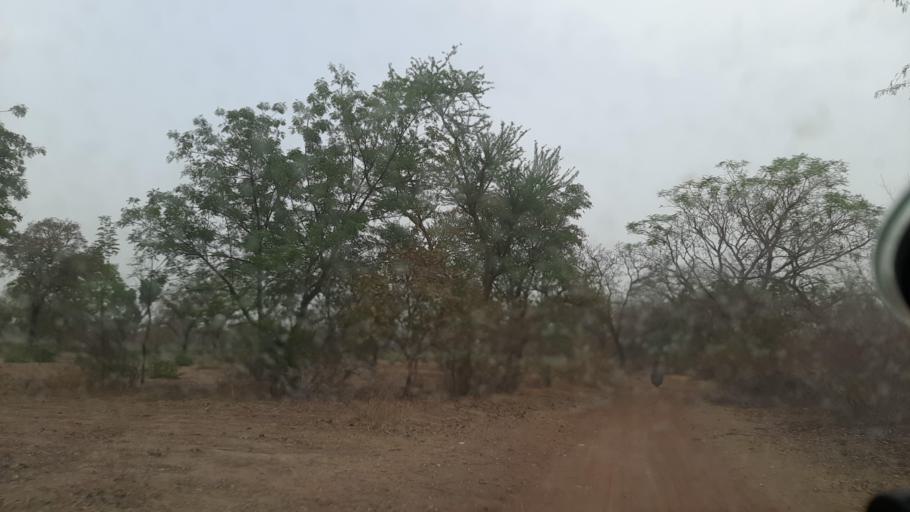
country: BF
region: Boucle du Mouhoun
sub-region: Province des Banwa
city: Salanso
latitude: 11.8494
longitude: -4.4230
